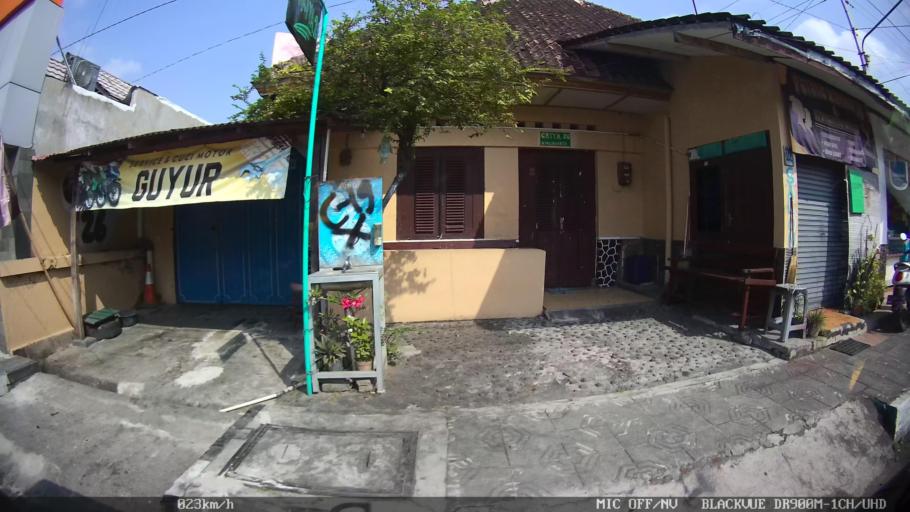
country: ID
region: Daerah Istimewa Yogyakarta
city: Yogyakarta
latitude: -7.8110
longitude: 110.3719
